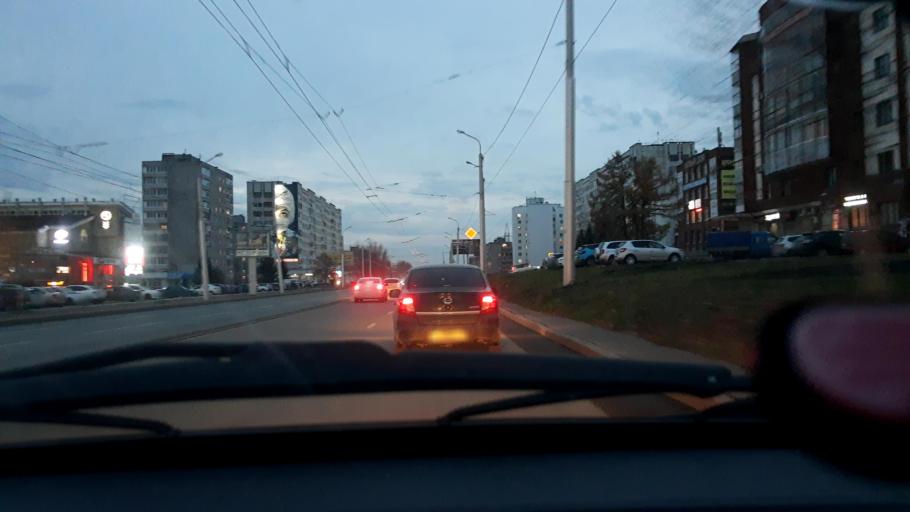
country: RU
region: Bashkortostan
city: Ufa
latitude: 54.7069
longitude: 55.9986
